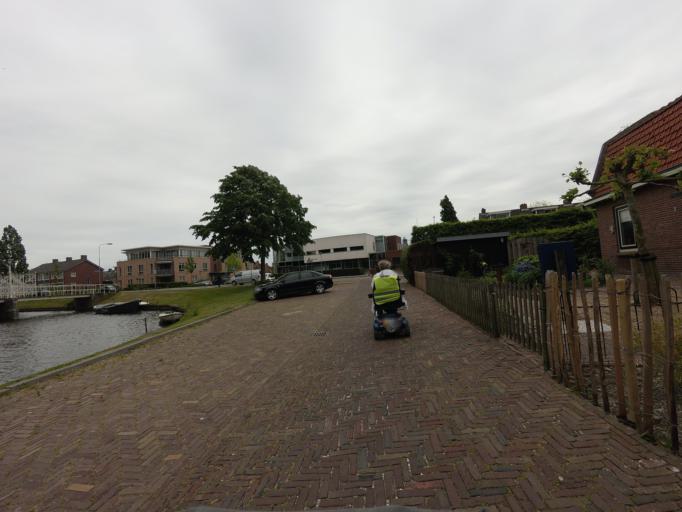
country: NL
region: North Holland
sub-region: Gemeente Medemblik
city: Medemblik
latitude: 52.7679
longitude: 5.1057
